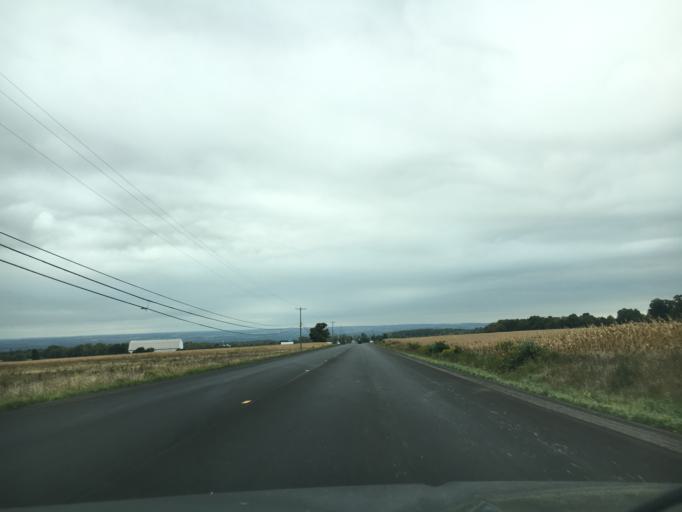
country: US
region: New York
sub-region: Cayuga County
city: Union Springs
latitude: 42.6814
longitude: -76.7977
